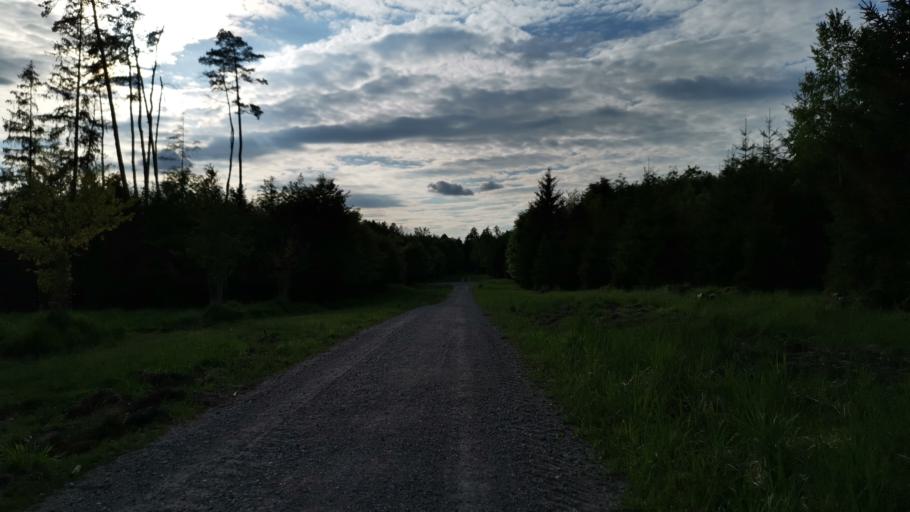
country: DE
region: Bavaria
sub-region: Upper Bavaria
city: Neuried
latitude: 48.0623
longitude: 11.4803
